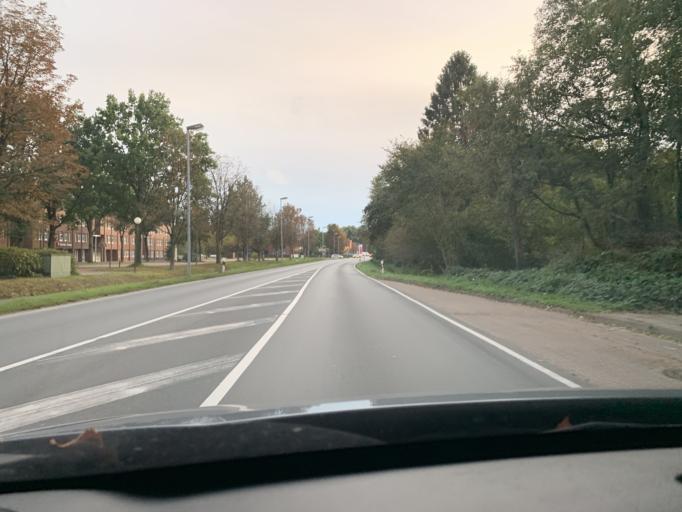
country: DE
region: Lower Saxony
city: Westerstede
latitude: 53.2547
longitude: 7.9334
